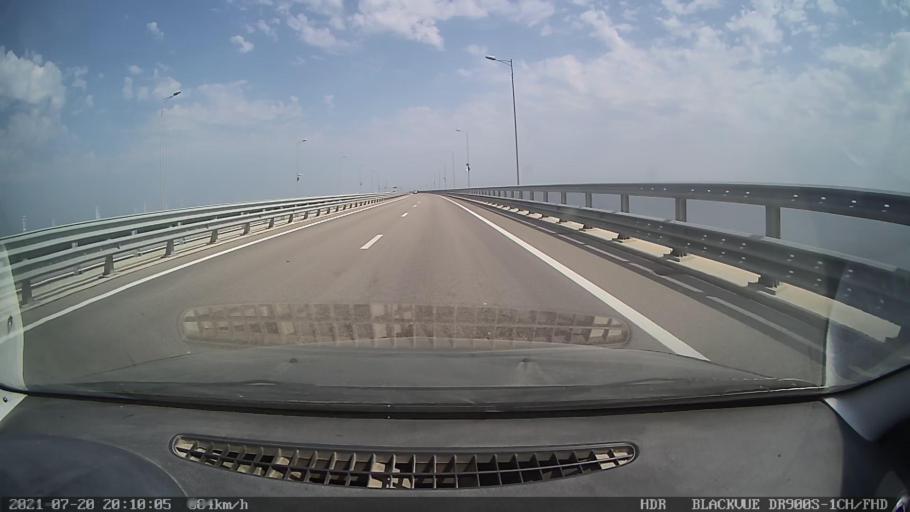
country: RU
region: Krasnodarskiy
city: Taman'
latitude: 45.2232
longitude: 36.6074
